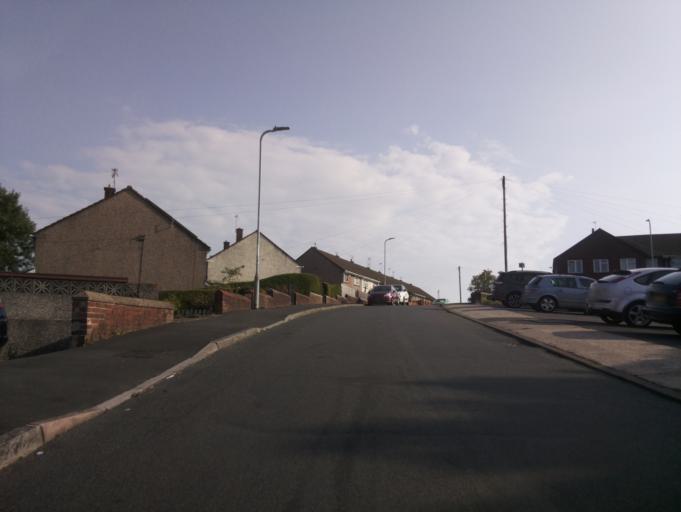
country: GB
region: Wales
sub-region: Newport
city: Newport
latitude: 51.6097
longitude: -3.0227
